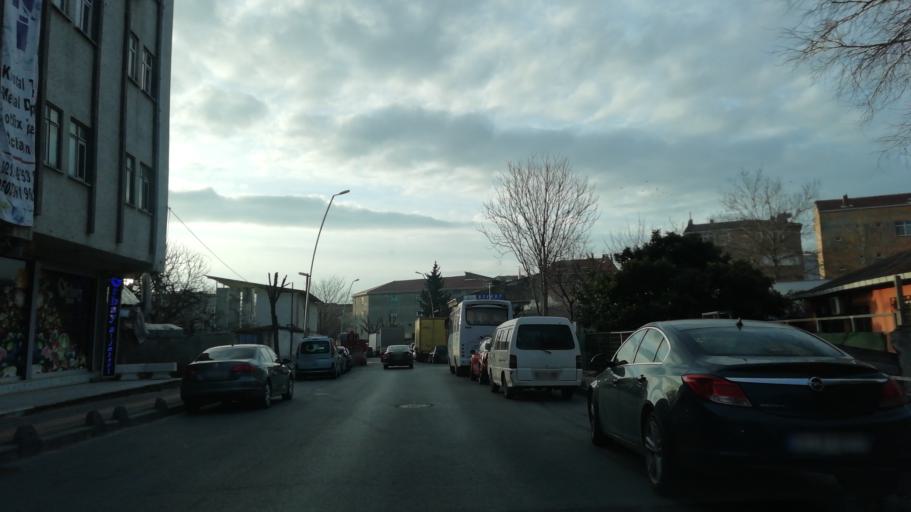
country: TR
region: Istanbul
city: Bahcelievler
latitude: 41.0118
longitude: 28.8256
